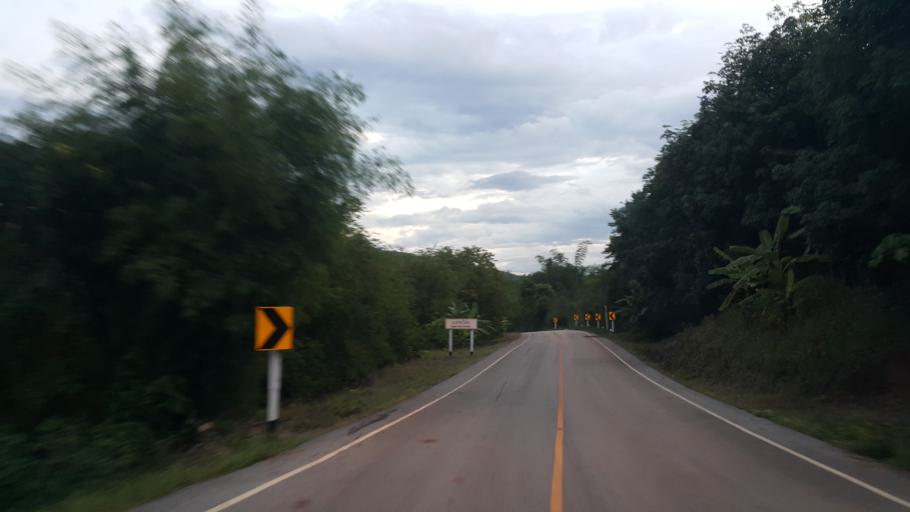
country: TH
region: Loei
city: Phu Ruea
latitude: 17.5126
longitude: 101.2326
